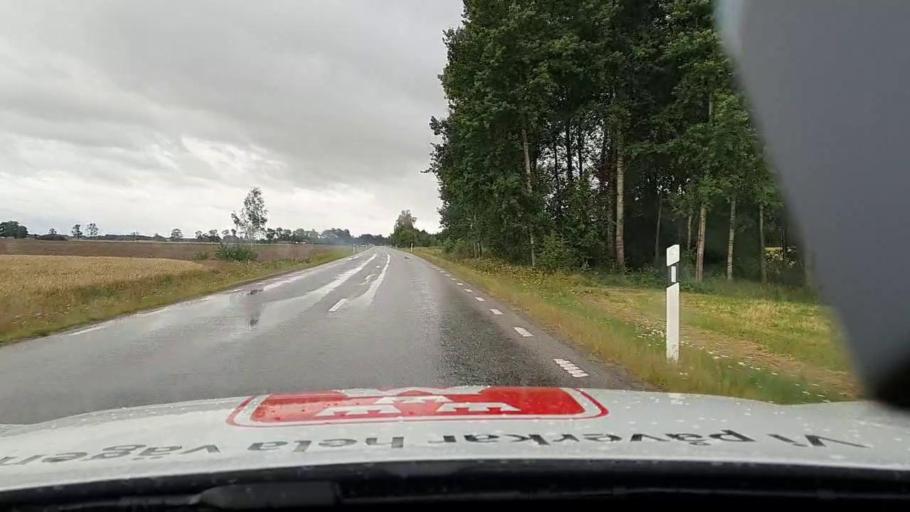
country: SE
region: Vaestra Goetaland
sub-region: Toreboda Kommun
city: Toereboda
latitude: 58.6376
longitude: 14.0275
